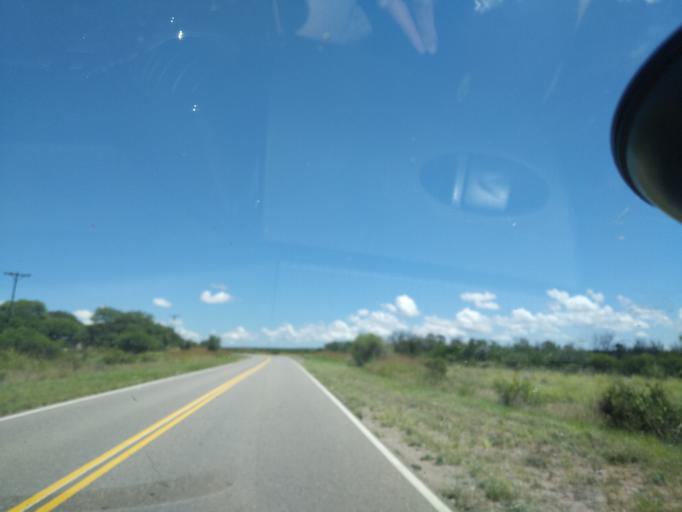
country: AR
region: Cordoba
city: Salsacate
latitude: -31.4089
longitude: -65.0963
